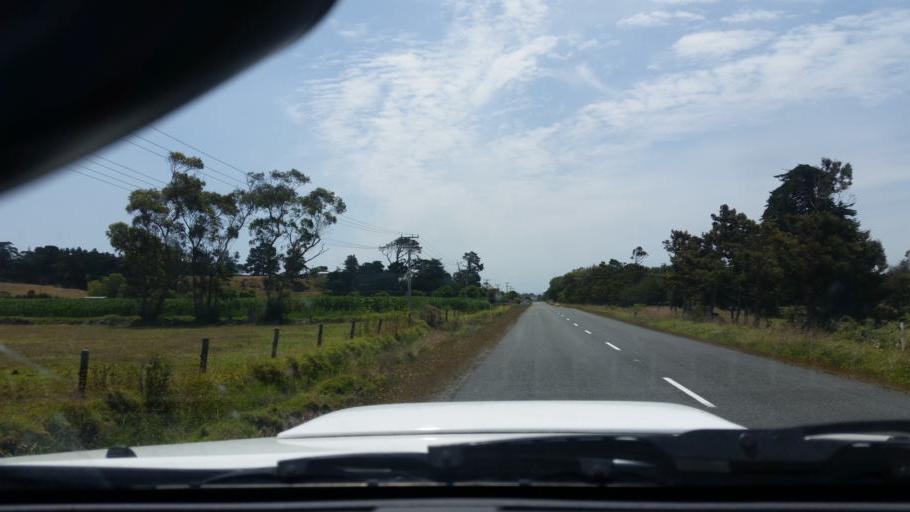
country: NZ
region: Northland
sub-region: Kaipara District
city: Dargaville
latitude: -36.0631
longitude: 173.9376
